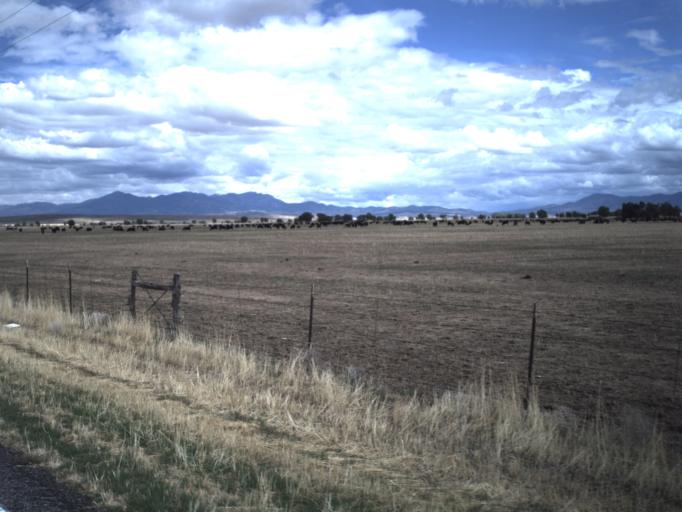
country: US
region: Utah
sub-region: Millard County
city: Fillmore
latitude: 39.0285
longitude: -112.4099
